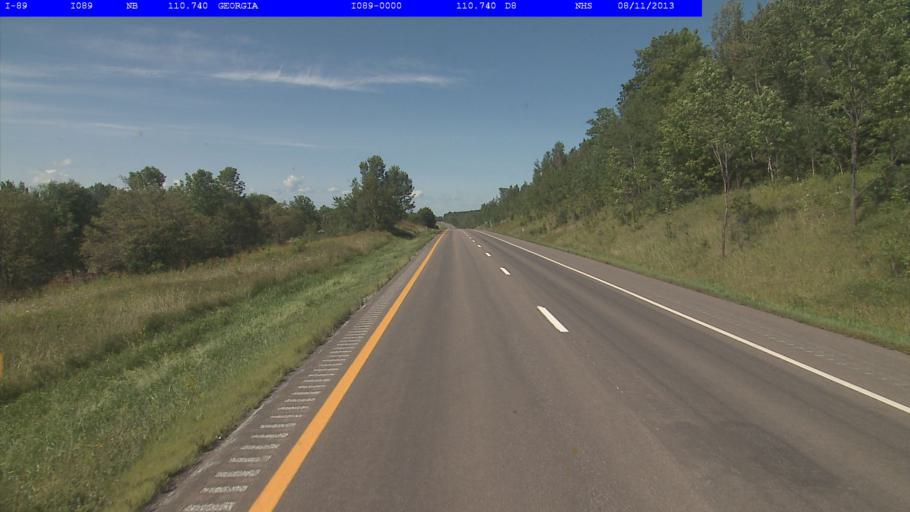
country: US
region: Vermont
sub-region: Franklin County
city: Saint Albans
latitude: 44.7519
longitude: -73.0778
